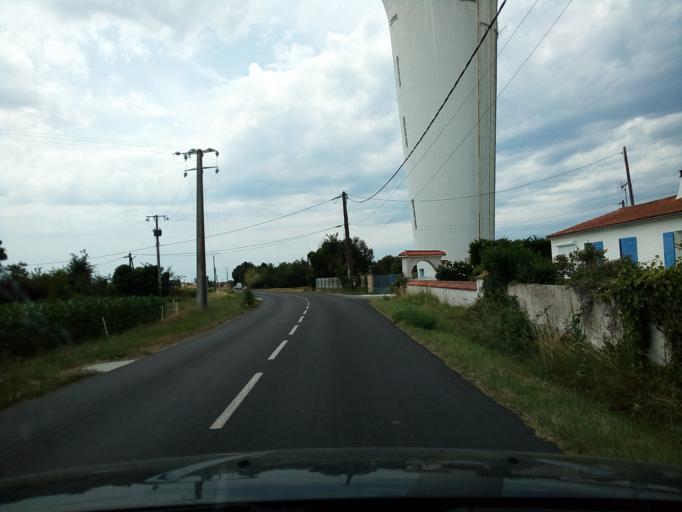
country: FR
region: Poitou-Charentes
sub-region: Departement de la Charente-Maritime
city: Dolus-d'Oleron
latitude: 45.9323
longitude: -1.3152
